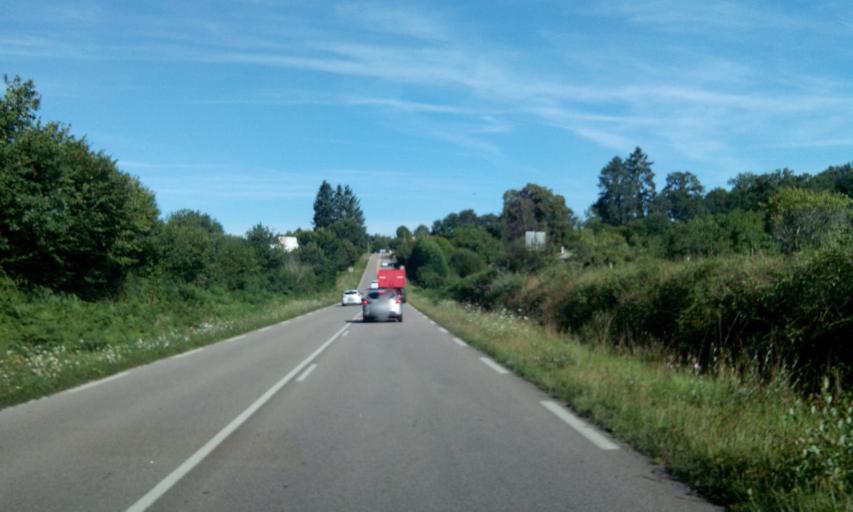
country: FR
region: Limousin
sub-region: Departement de la Haute-Vienne
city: Saint-Leonard-de-Noblat
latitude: 45.8439
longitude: 1.4611
